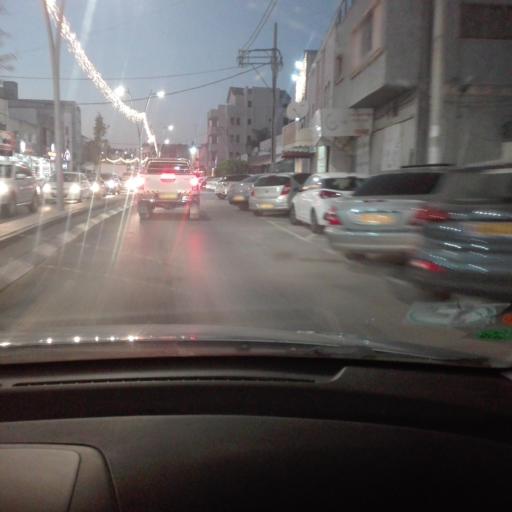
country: PS
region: West Bank
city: Nazlat `Isa
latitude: 32.4161
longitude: 35.0460
